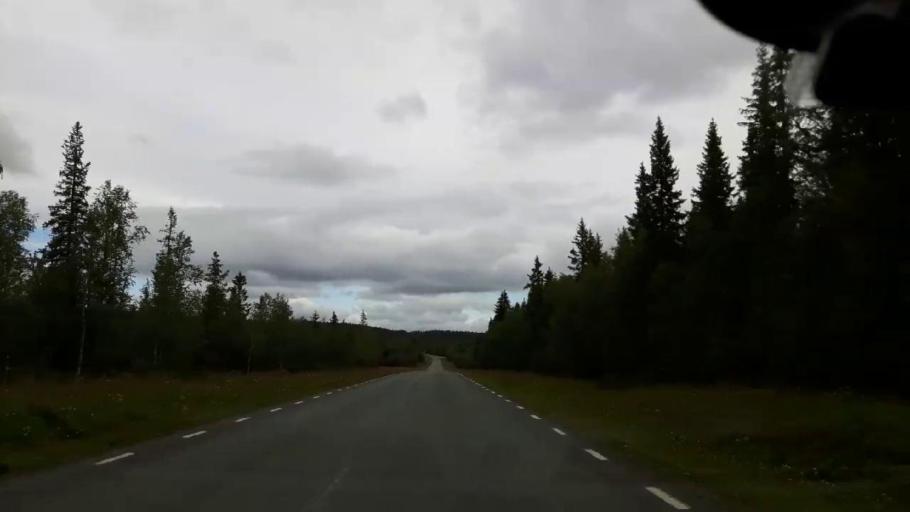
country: SE
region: Jaemtland
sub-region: Krokoms Kommun
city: Valla
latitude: 63.5633
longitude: 13.8457
